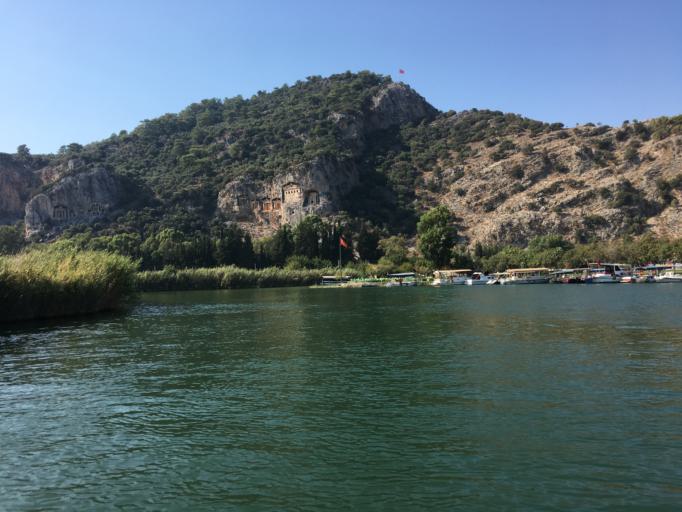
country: TR
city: Dalyan
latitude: 36.8311
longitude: 28.6379
